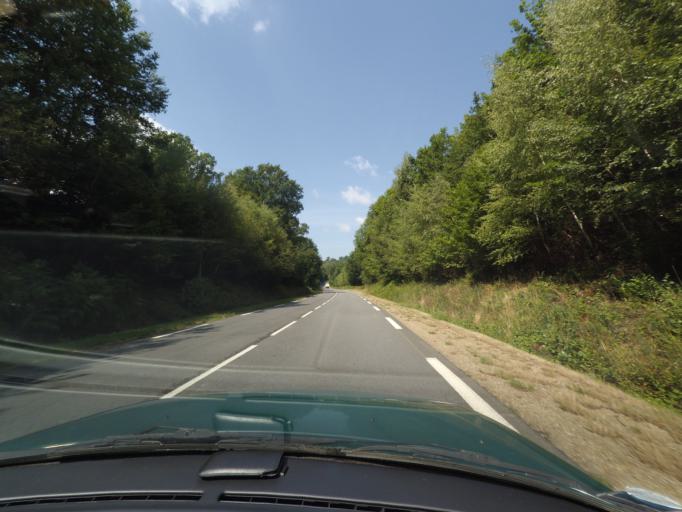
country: FR
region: Limousin
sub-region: Departement de la Haute-Vienne
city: Saint-Leonard-de-Noblat
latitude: 45.7776
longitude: 1.5072
